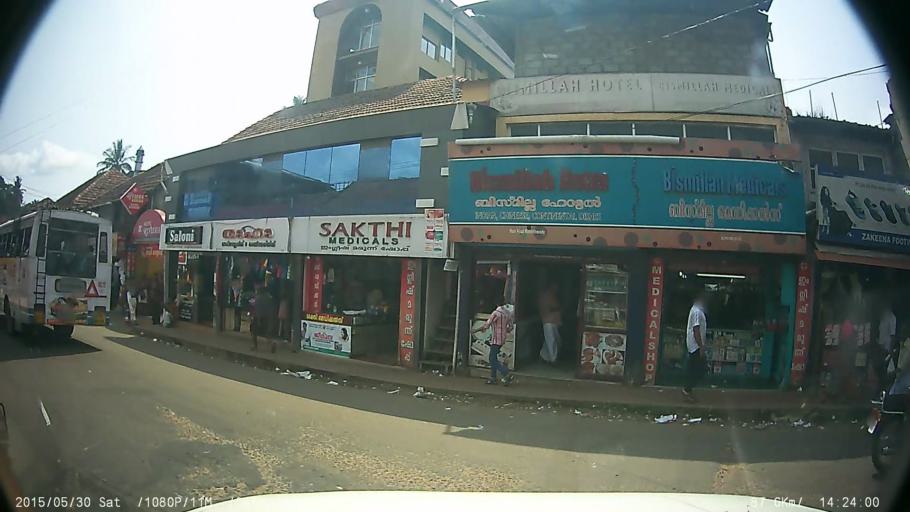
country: IN
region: Kerala
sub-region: Wayanad
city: Panamaram
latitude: 11.8030
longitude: 76.0037
